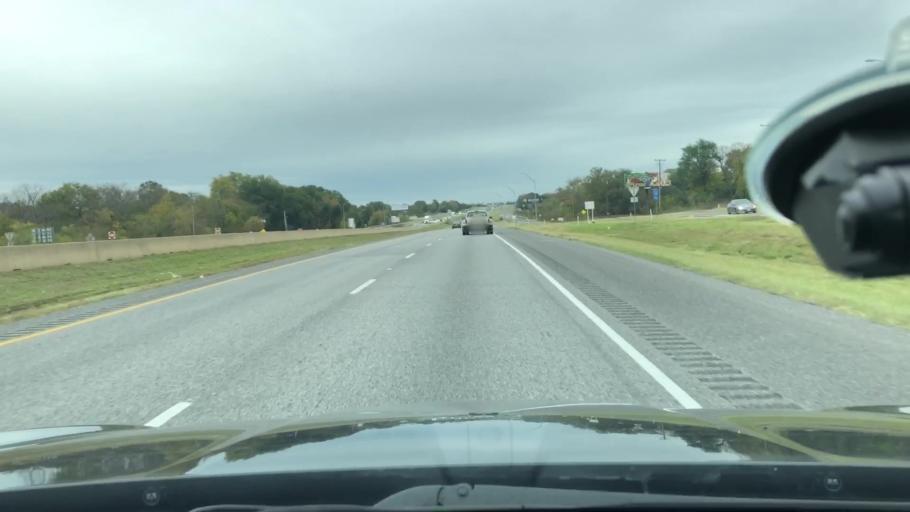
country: US
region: Texas
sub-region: Hunt County
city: Greenville
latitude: 33.1332
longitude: -96.0547
